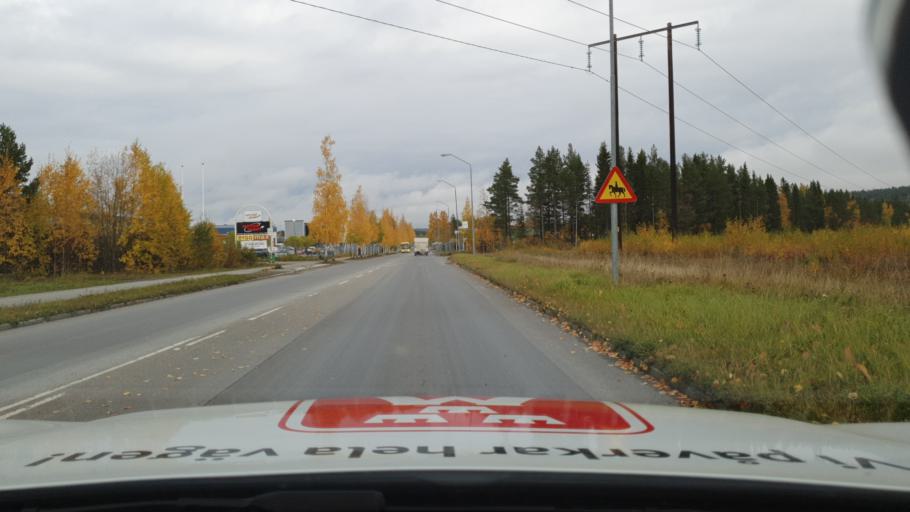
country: SE
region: Jaemtland
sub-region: OEstersunds Kommun
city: Ostersund
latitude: 63.1645
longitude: 14.6891
